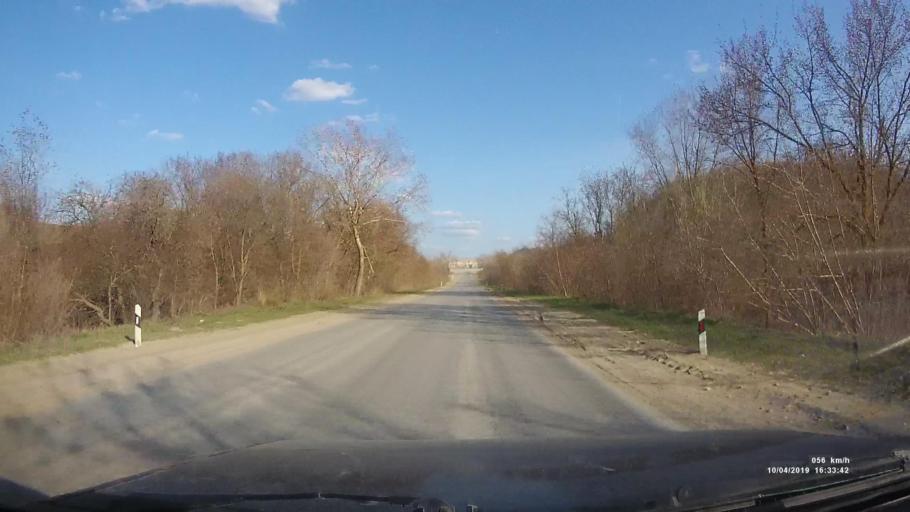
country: RU
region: Rostov
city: Staraya Stanitsa
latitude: 48.2399
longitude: 40.4004
